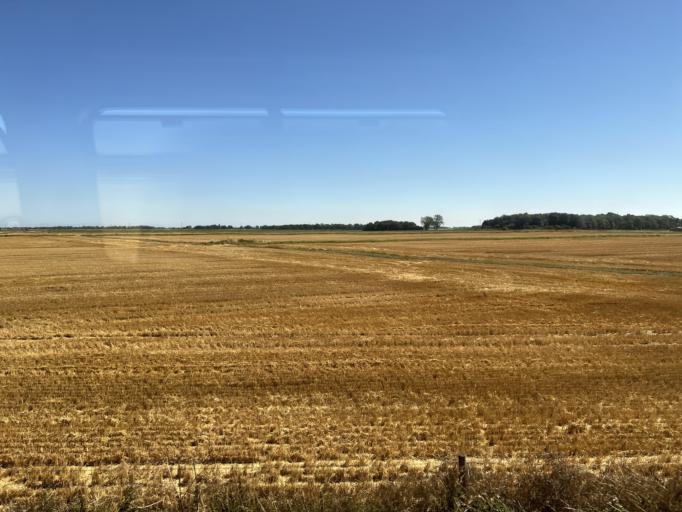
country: GB
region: England
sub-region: Lincolnshire
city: Spilsby
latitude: 53.1173
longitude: 0.1326
